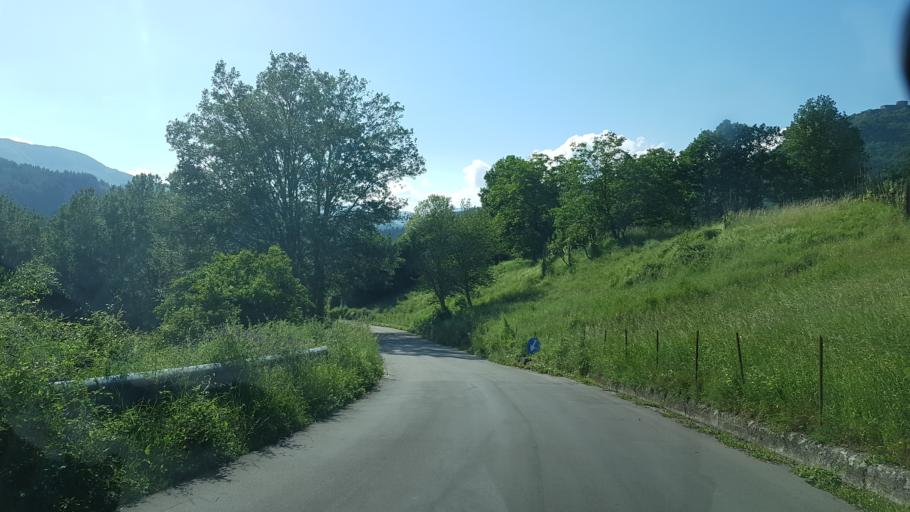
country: IT
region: Tuscany
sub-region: Provincia di Lucca
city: San Romano in Garfagnana
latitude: 44.1663
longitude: 10.3421
